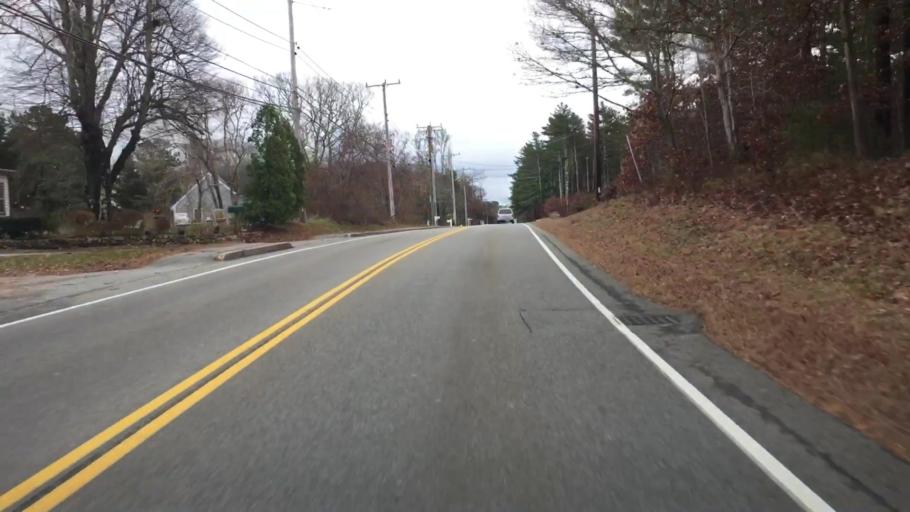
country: US
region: Massachusetts
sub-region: Barnstable County
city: Teaticket
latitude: 41.5793
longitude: -70.6043
